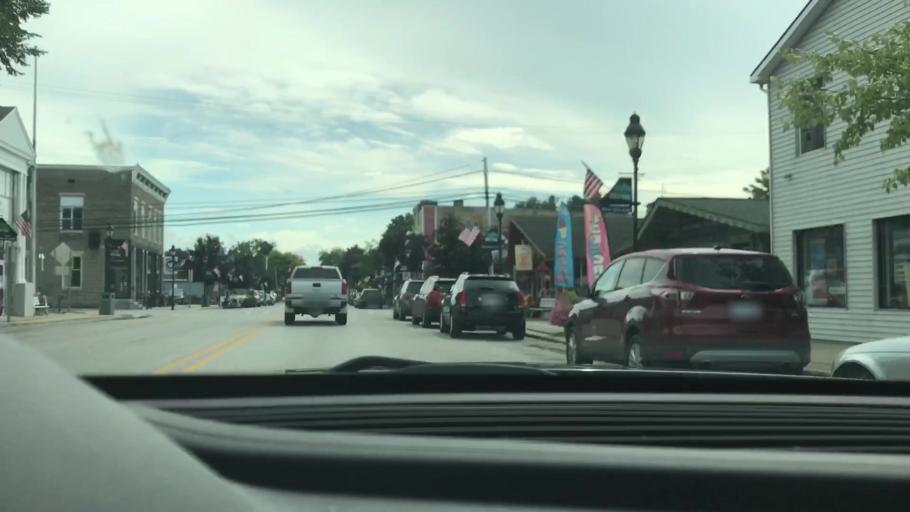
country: US
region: Michigan
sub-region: Antrim County
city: Bellaire
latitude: 44.9770
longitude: -85.2099
